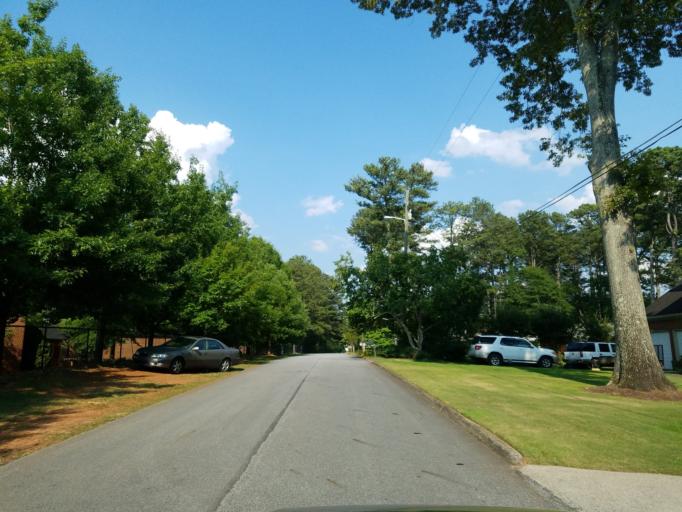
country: US
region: Georgia
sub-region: Cobb County
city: Marietta
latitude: 33.9453
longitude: -84.4882
